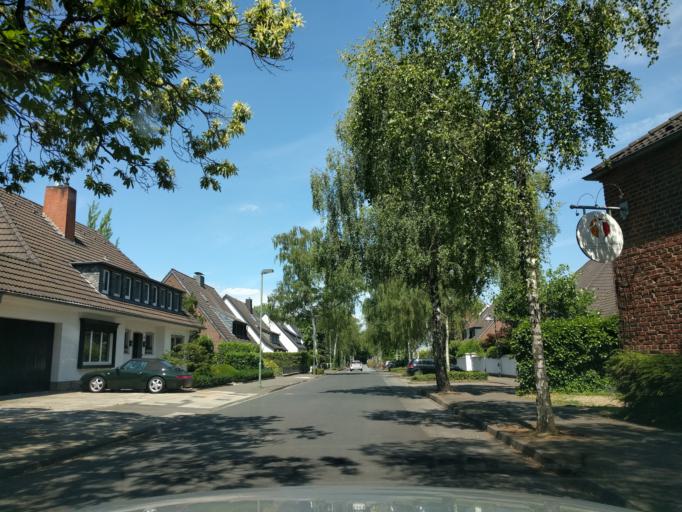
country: DE
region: North Rhine-Westphalia
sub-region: Regierungsbezirk Dusseldorf
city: Meerbusch
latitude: 51.2501
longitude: 6.7033
